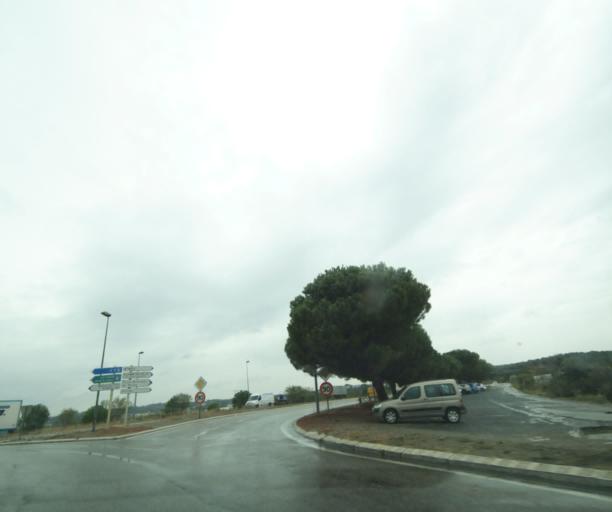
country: FR
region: Languedoc-Roussillon
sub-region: Departement du Gard
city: Marguerittes
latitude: 43.8575
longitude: 4.4189
